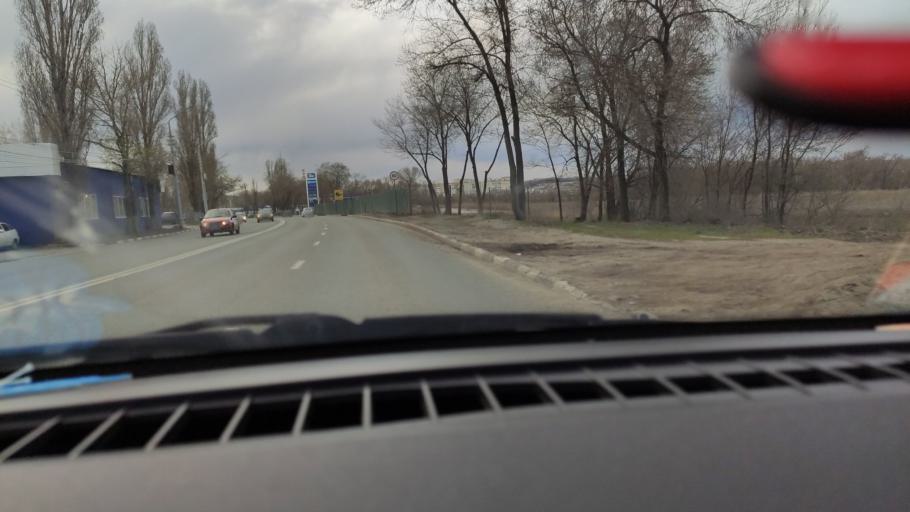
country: RU
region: Saratov
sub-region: Saratovskiy Rayon
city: Saratov
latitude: 51.5796
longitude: 45.9822
